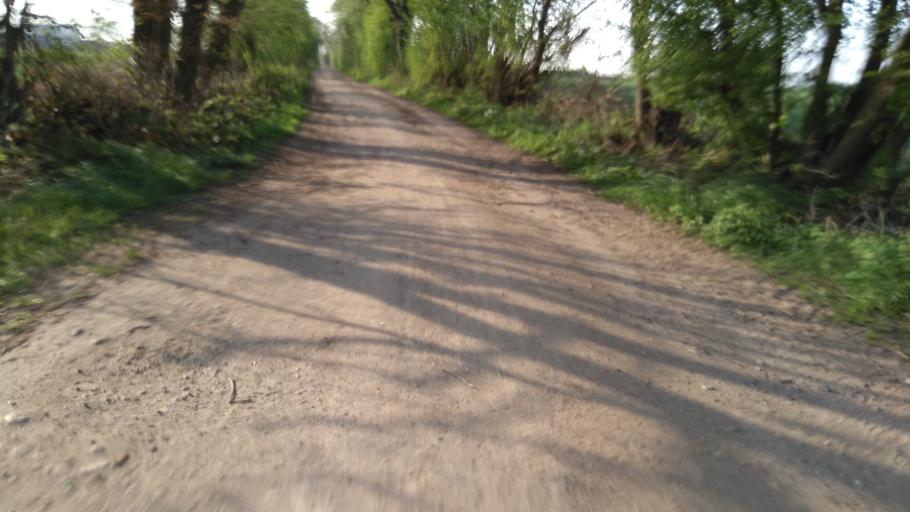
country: DE
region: Lower Saxony
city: Apensen
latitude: 53.4407
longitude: 9.6357
